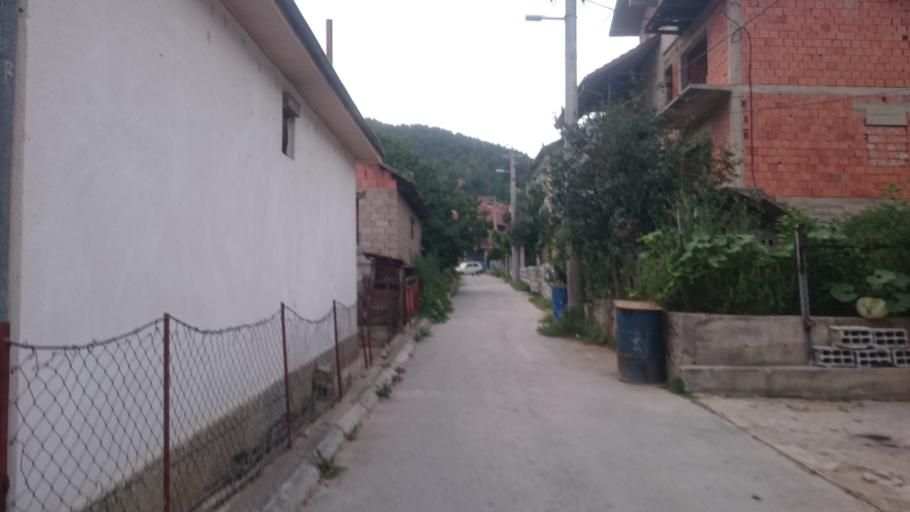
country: MK
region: Makedonski Brod
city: Makedonski Brod
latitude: 41.5171
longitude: 21.2138
